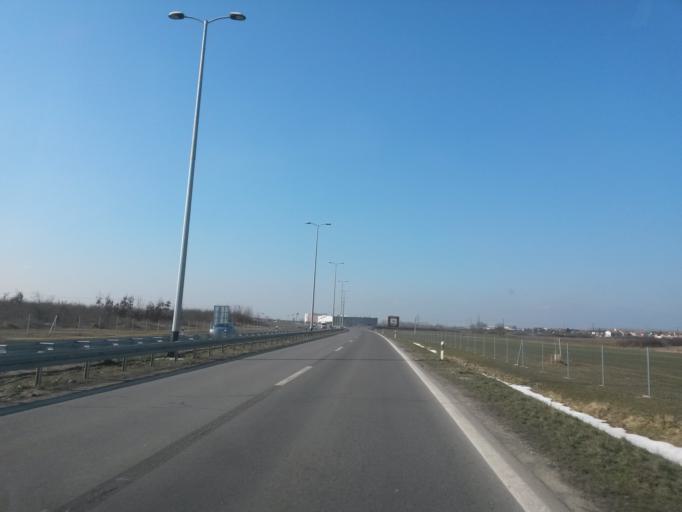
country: HR
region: Osjecko-Baranjska
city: Brijest
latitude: 45.5510
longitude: 18.6526
